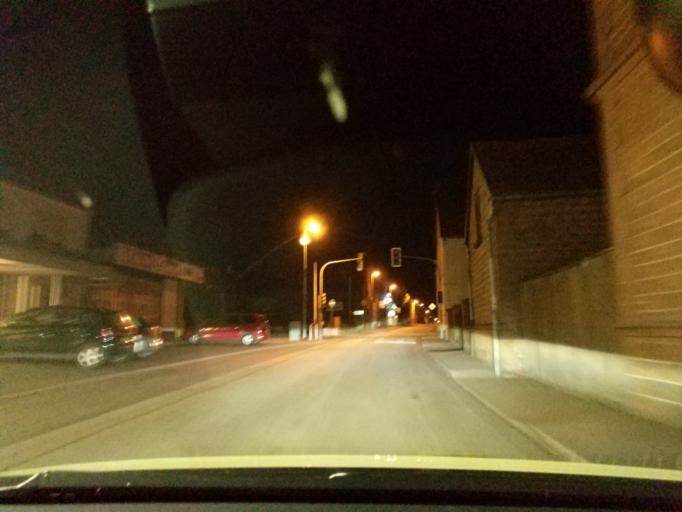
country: DE
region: Rheinland-Pfalz
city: Weilerbach
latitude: 49.4805
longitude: 7.6333
